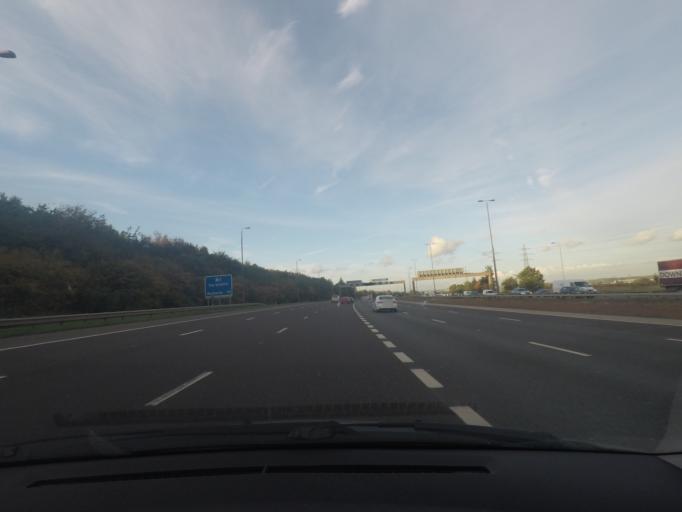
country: GB
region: England
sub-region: City and Borough of Leeds
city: Lofthouse
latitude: 53.7484
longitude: -1.5175
